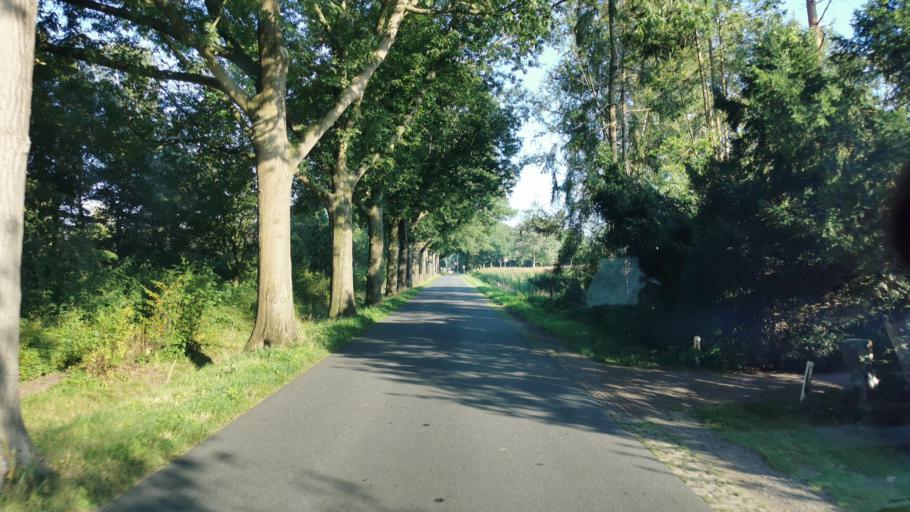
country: NL
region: Overijssel
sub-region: Gemeente Oldenzaal
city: Oldenzaal
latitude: 52.3170
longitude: 6.8913
